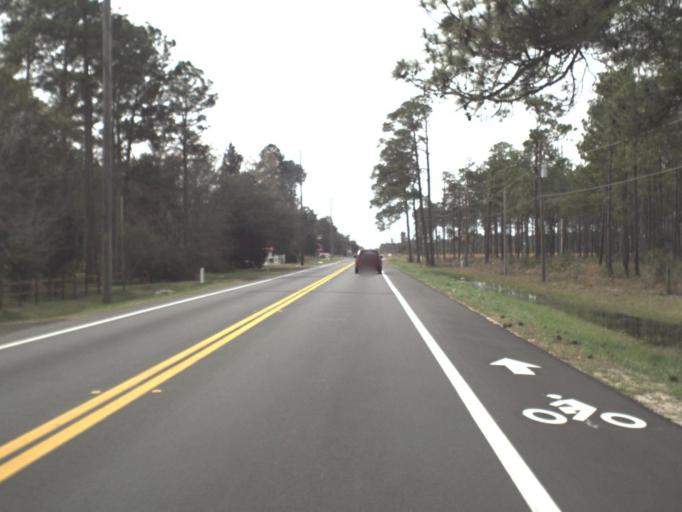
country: US
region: Florida
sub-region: Gadsden County
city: Midway
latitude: 30.4433
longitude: -84.4076
